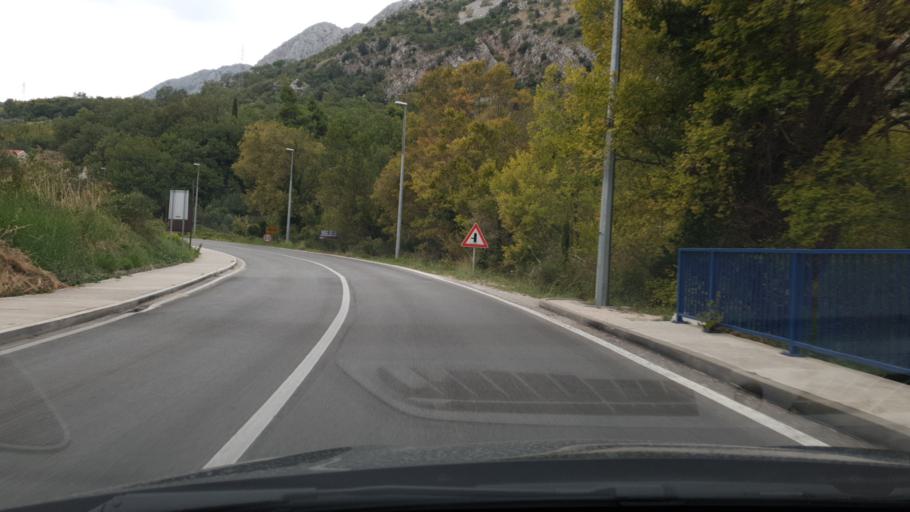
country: HR
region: Dubrovacko-Neretvanska
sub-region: Grad Dubrovnik
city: Mokosica
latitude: 42.6740
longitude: 18.1359
